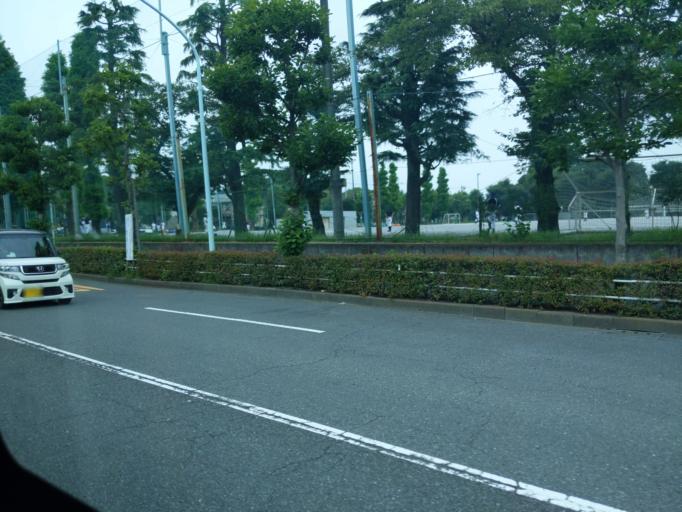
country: JP
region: Saitama
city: Wako
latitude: 35.7878
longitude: 139.6522
